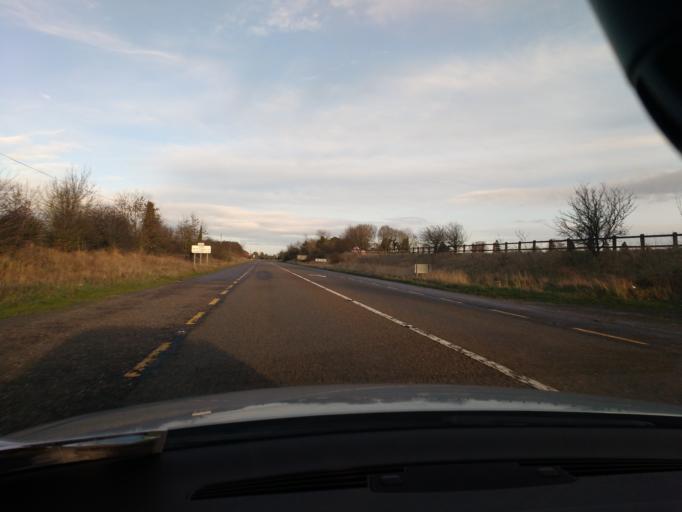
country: IE
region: Munster
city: Thurles
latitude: 52.6714
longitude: -7.6808
